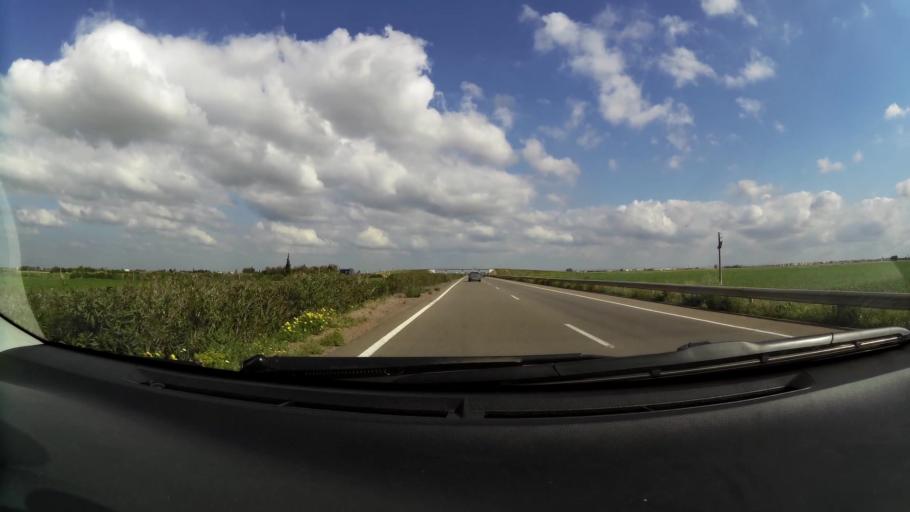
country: MA
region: Chaouia-Ouardigha
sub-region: Settat Province
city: Berrechid
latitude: 33.3088
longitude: -7.5890
